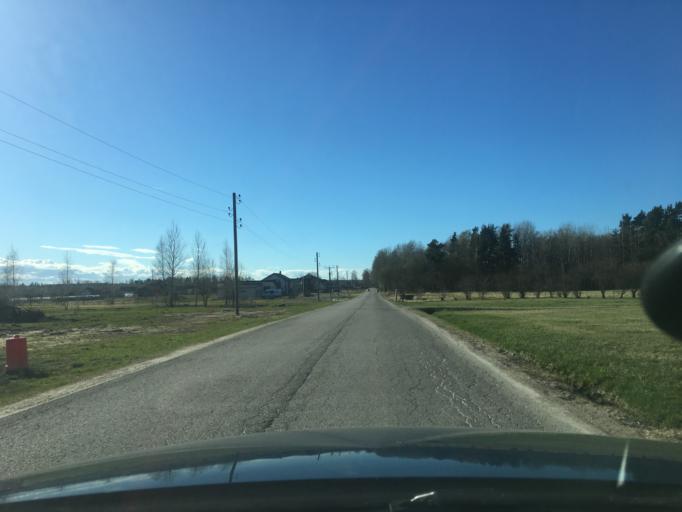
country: LV
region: Salaspils
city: Salaspils
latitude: 56.8730
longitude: 24.3383
